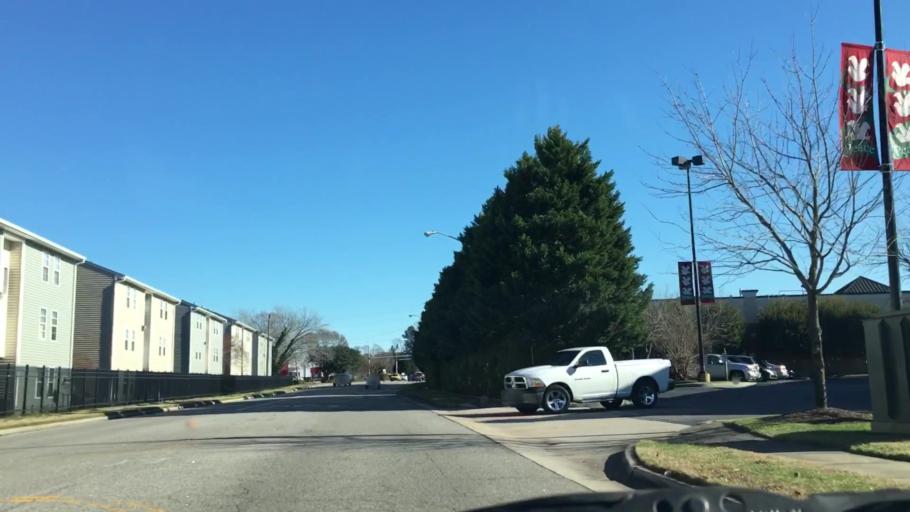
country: US
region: Virginia
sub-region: City of Virginia Beach
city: Virginia Beach
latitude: 36.8523
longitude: -76.0255
